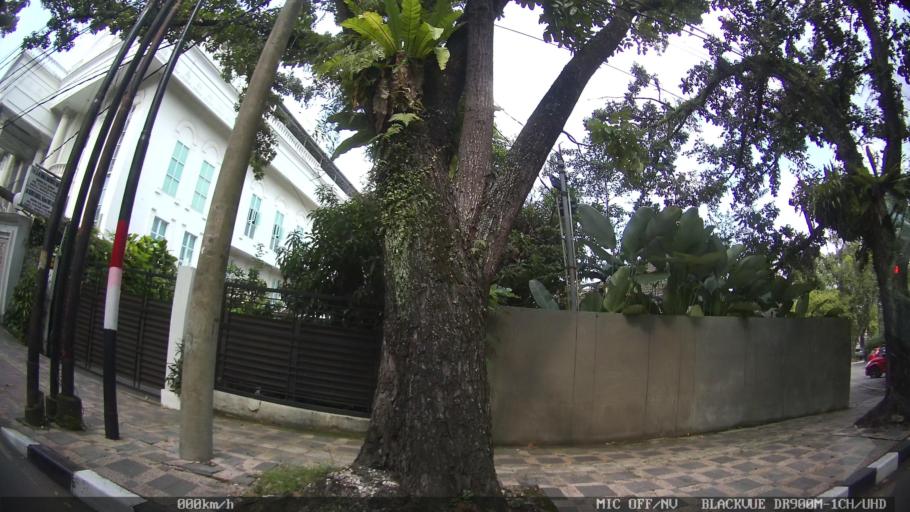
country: ID
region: North Sumatra
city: Medan
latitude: 3.5758
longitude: 98.6700
